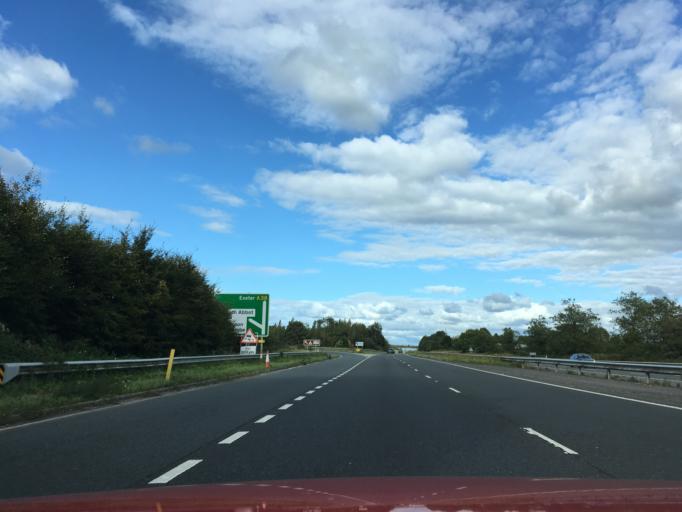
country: GB
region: England
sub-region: Devon
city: Ashburton
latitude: 50.5331
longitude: -3.7195
